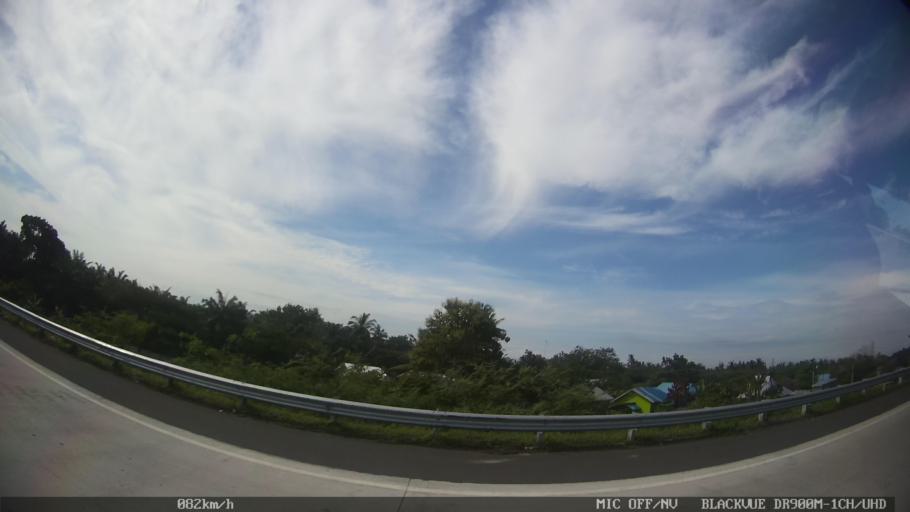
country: ID
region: North Sumatra
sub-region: Kabupaten Langkat
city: Stabat
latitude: 3.7134
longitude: 98.5079
